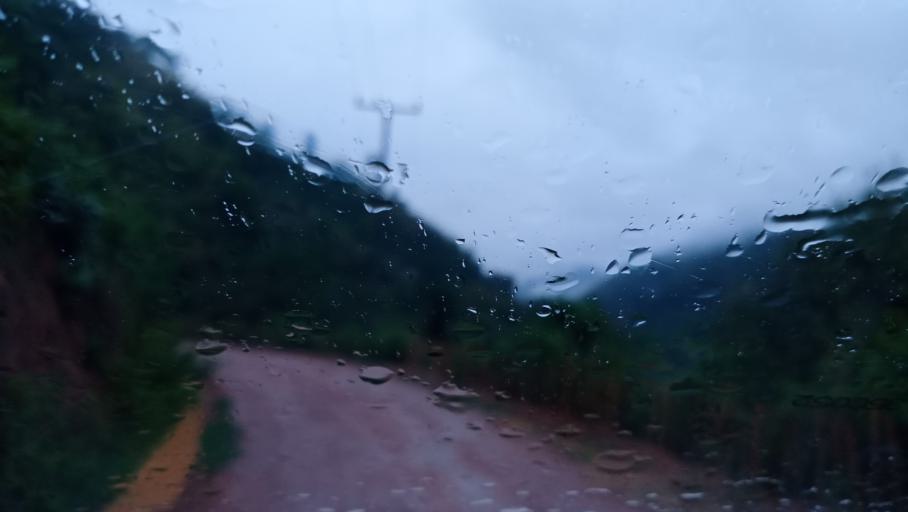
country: LA
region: Phongsali
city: Khoa
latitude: 21.1446
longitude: 102.3246
